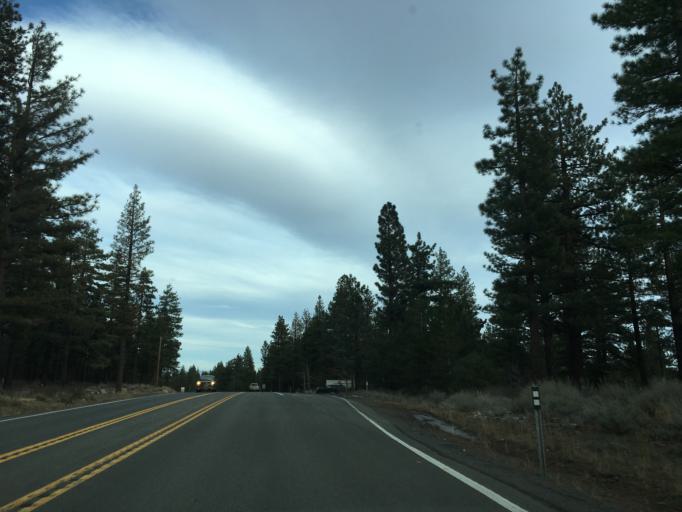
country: US
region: Nevada
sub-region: Washoe County
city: Incline Village
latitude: 39.3590
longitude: -119.8544
